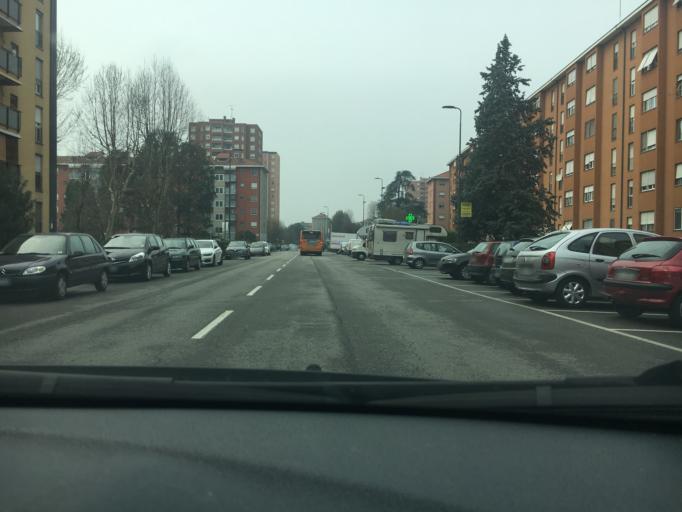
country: IT
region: Lombardy
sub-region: Citta metropolitana di Milano
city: Pero
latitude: 45.4920
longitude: 9.1125
